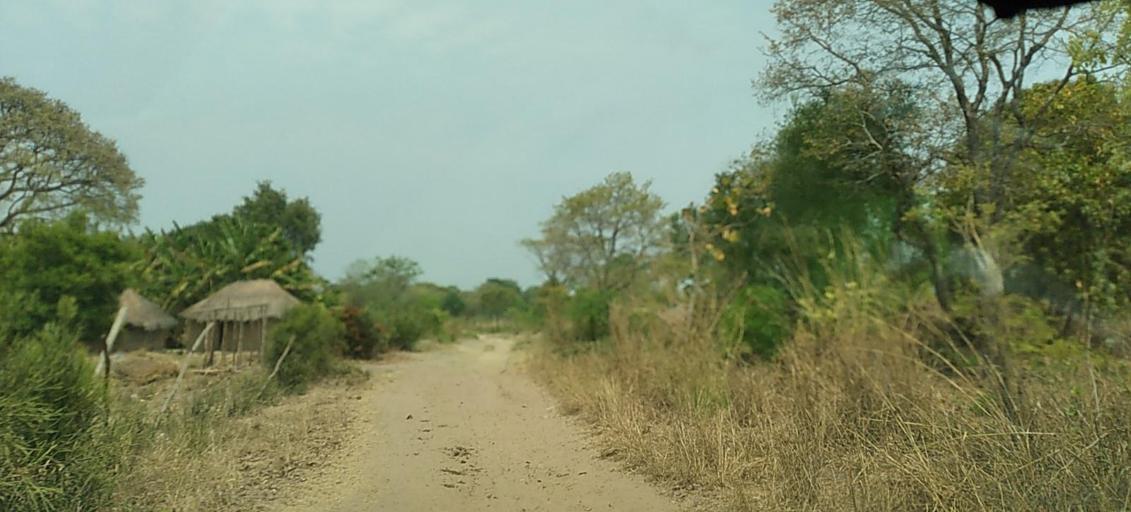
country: ZM
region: North-Western
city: Kabompo
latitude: -13.5342
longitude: 24.4586
